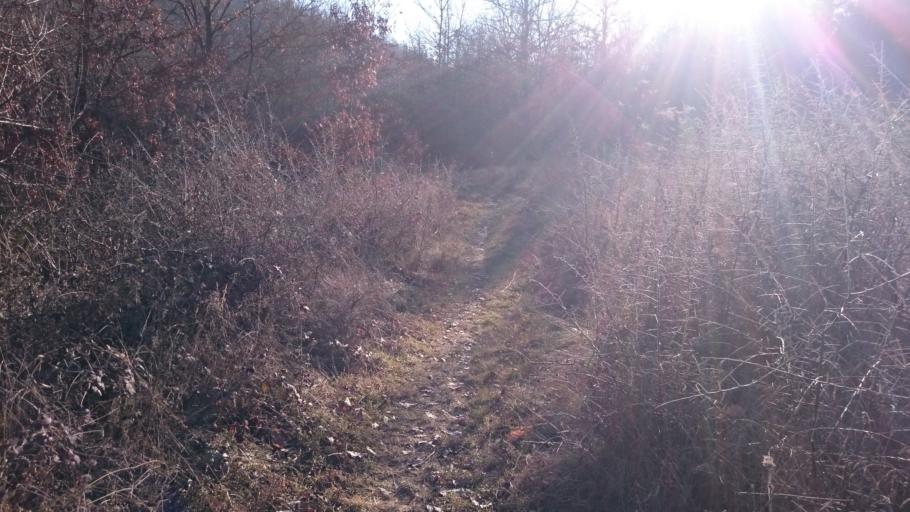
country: MK
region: Makedonski Brod
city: Makedonski Brod
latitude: 41.5129
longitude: 21.2278
